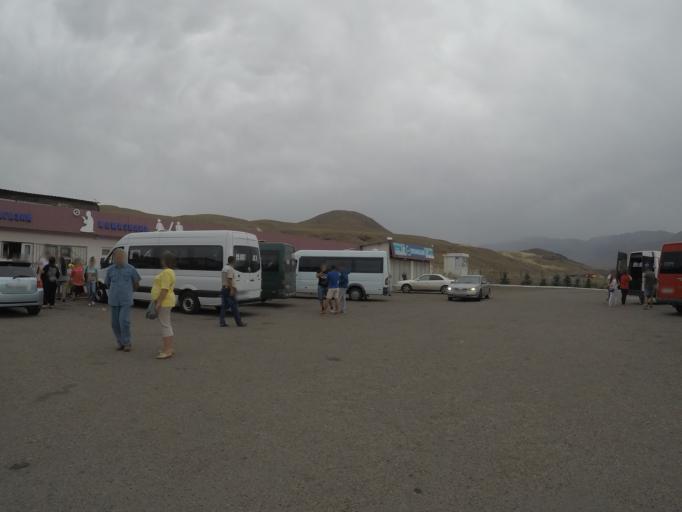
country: KG
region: Naryn
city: Kochkor
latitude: 42.5090
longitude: 75.8336
